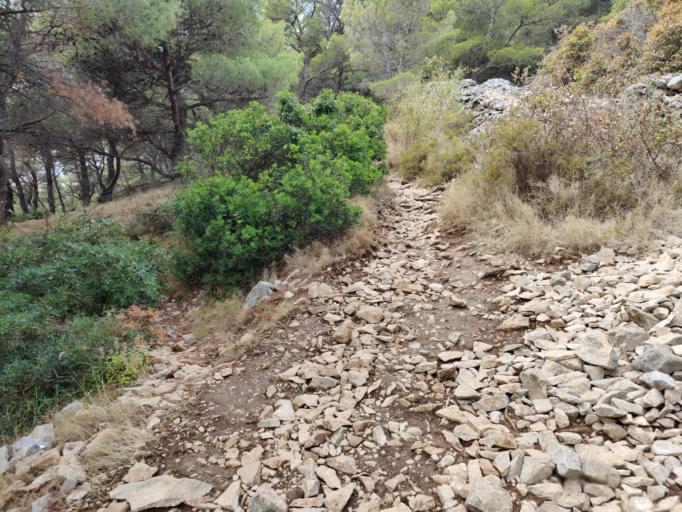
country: HR
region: Splitsko-Dalmatinska
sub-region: Grad Hvar
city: Hvar
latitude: 43.1638
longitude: 16.4546
